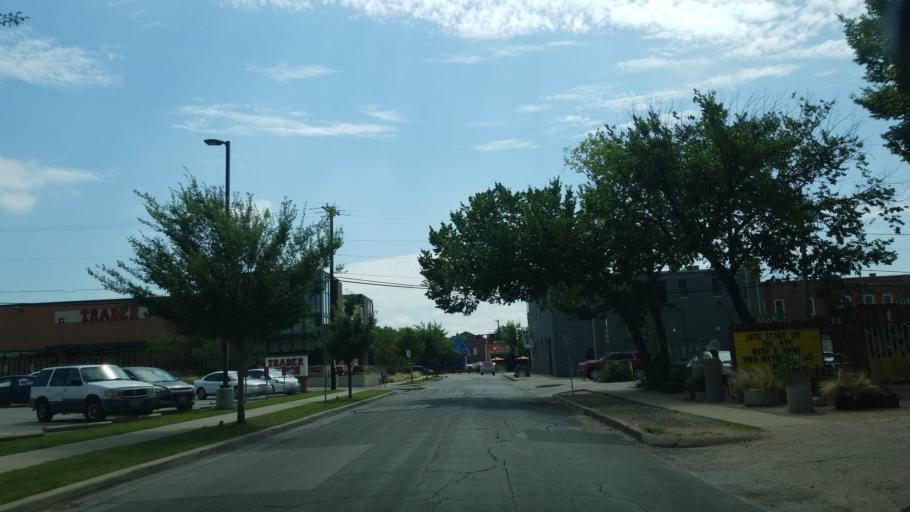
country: US
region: Texas
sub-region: Dallas County
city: Highland Park
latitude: 32.8146
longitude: -96.7714
